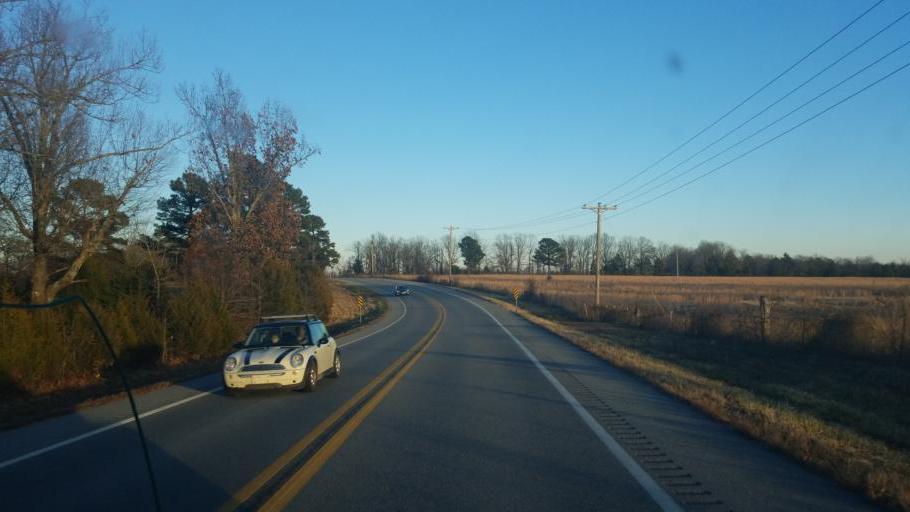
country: US
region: Arkansas
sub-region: Baxter County
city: Mountain Home
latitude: 36.3756
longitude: -92.1392
